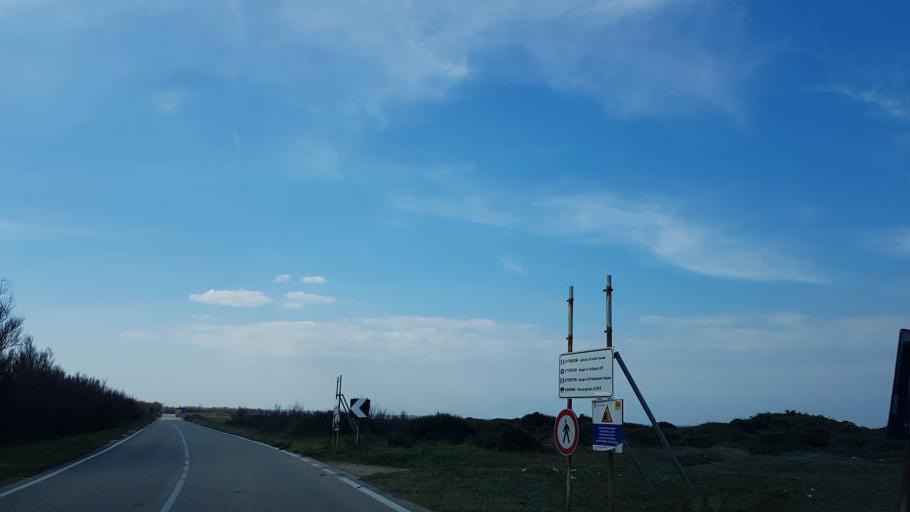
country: IT
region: Apulia
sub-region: Provincia di Brindisi
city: Brindisi
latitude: 40.6884
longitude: 17.8535
